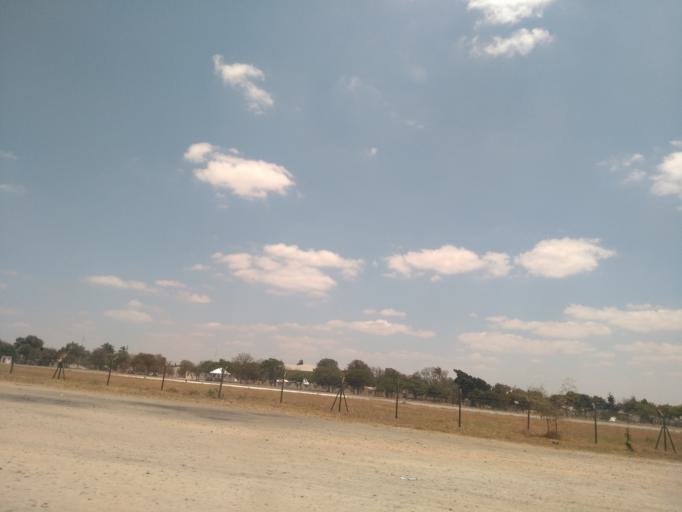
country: TZ
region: Dodoma
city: Dodoma
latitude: -6.1713
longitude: 35.7478
